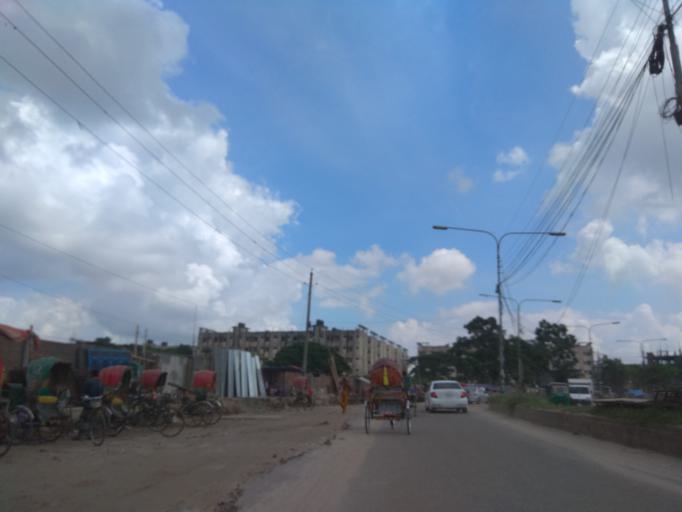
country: BD
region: Dhaka
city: Paltan
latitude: 23.8041
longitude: 90.3875
